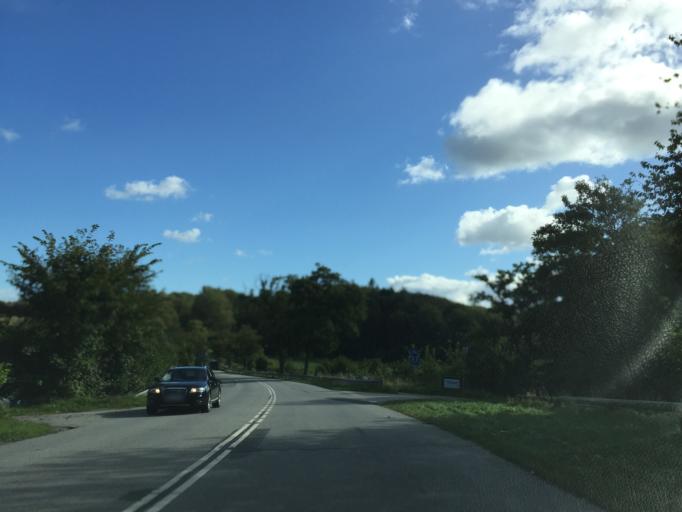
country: DK
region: Central Jutland
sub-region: Viborg Kommune
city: Viborg
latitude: 56.4448
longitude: 9.4544
